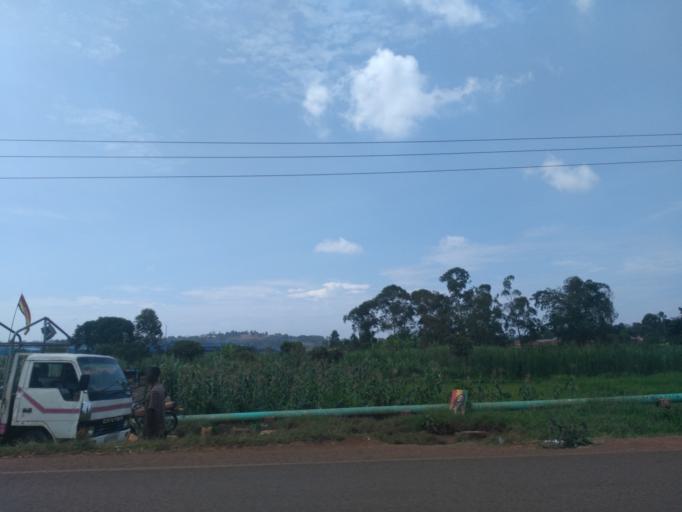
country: UG
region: Eastern Region
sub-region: Jinja District
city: Bugembe
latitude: 0.4624
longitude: 33.2278
